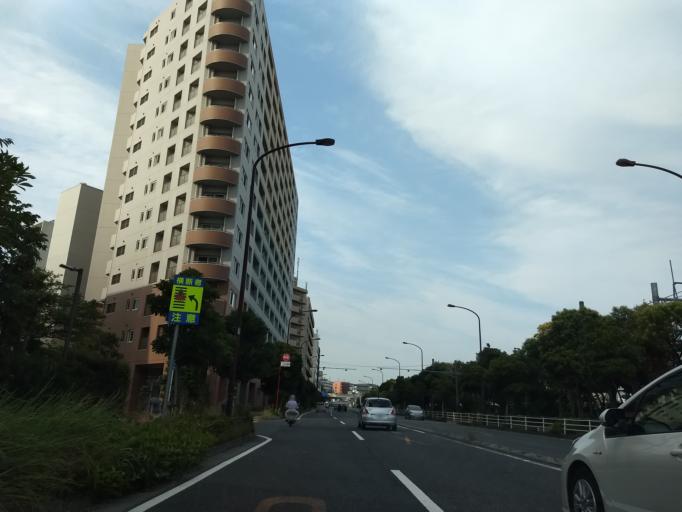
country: JP
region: Kanagawa
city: Yokohama
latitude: 35.4793
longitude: 139.6338
